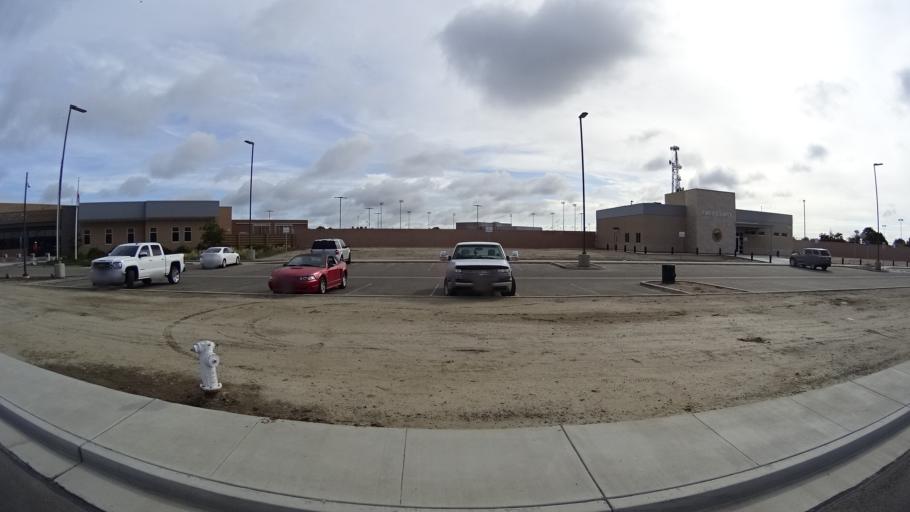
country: US
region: California
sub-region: Kings County
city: Hanford
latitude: 36.3322
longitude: -119.6693
